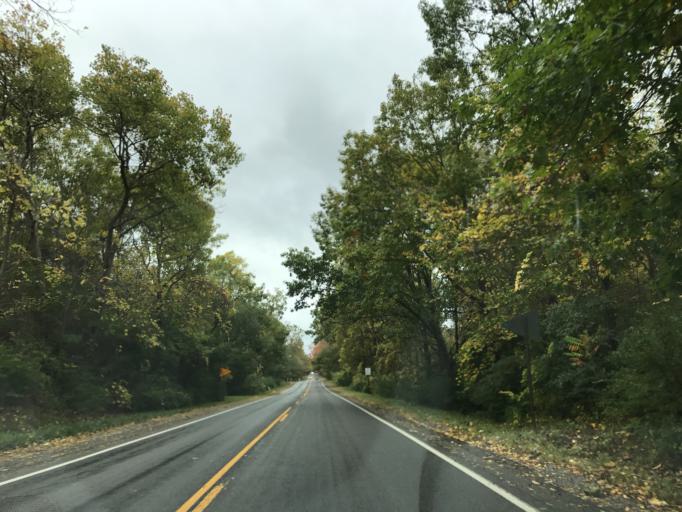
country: US
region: Michigan
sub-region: Washtenaw County
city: Ann Arbor
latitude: 42.3207
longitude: -83.6615
